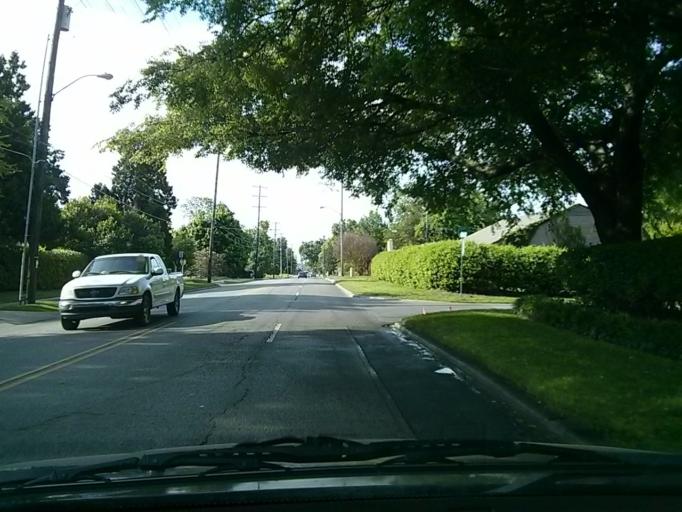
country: US
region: Oklahoma
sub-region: Tulsa County
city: Tulsa
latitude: 36.1231
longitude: -95.9757
